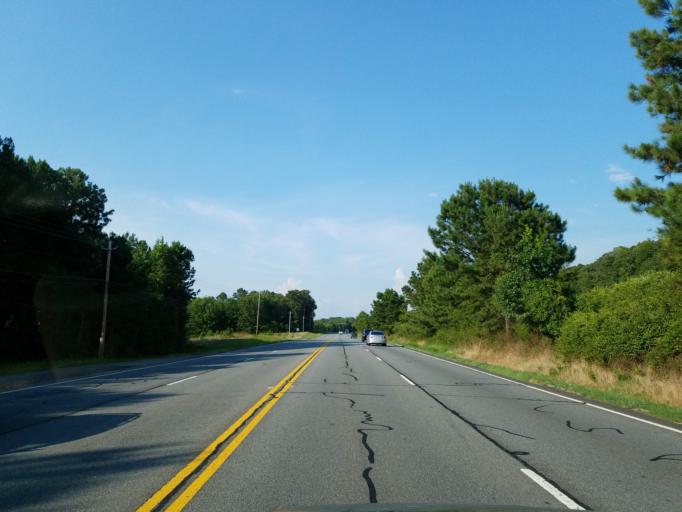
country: US
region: Georgia
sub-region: Bartow County
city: Cartersville
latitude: 34.2544
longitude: -84.7671
